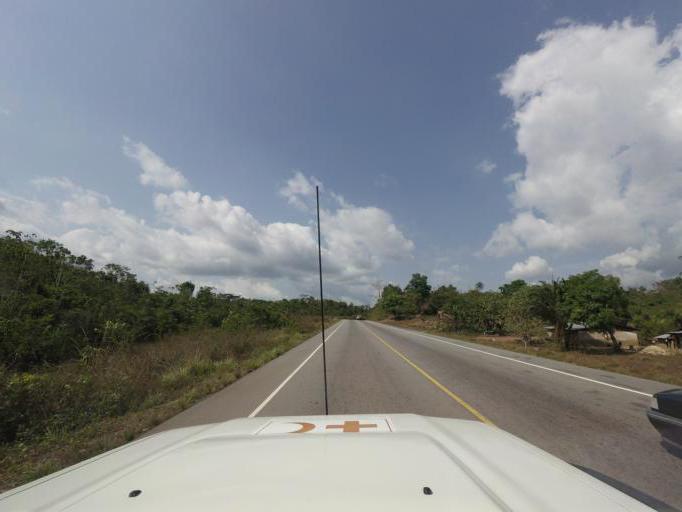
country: LR
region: Bong
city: Gbarnga
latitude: 6.8240
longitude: -9.8710
